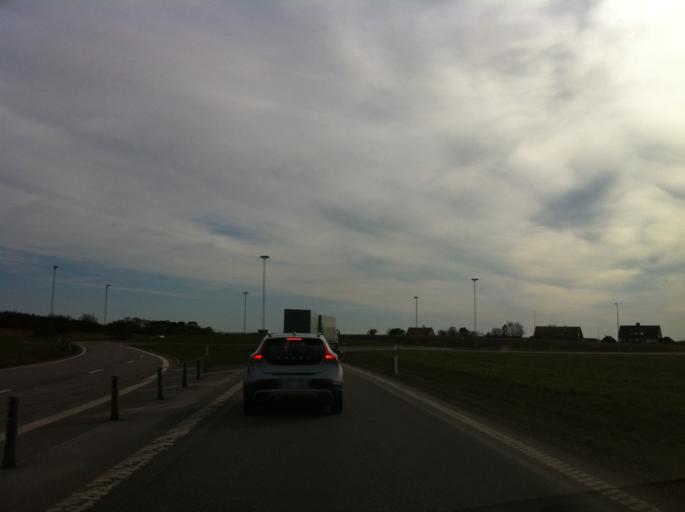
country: SE
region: Skane
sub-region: Hoganas Kommun
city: Hoganas
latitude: 56.1393
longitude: 12.5923
